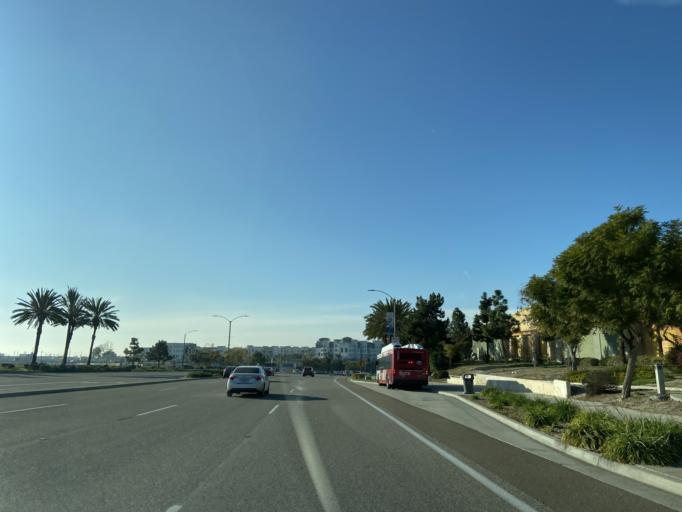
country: US
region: California
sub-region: San Diego County
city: Bonita
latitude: 32.6279
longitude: -116.9650
